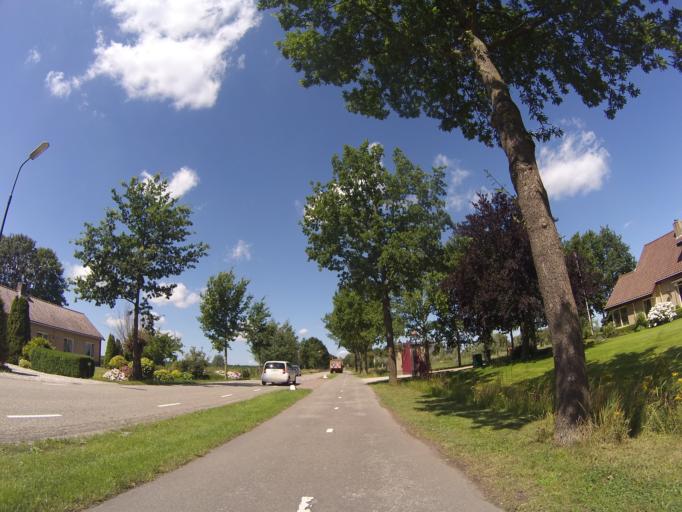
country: NL
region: Utrecht
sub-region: Stichtse Vecht
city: Spechtenkamp
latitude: 52.1144
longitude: 5.0138
